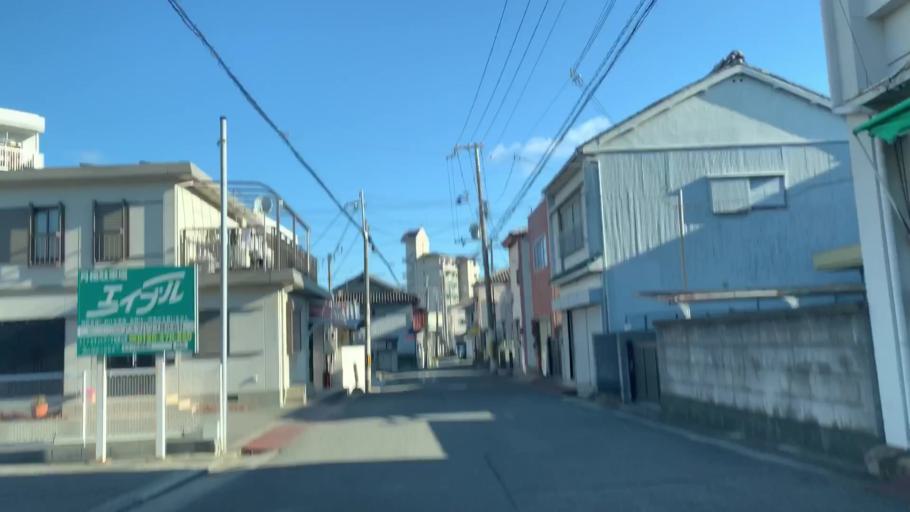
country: JP
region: Wakayama
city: Wakayama-shi
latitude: 34.2412
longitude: 135.1829
